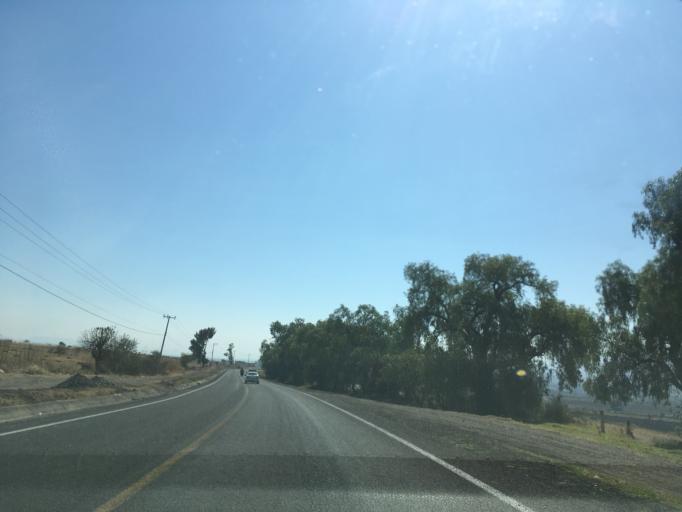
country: MX
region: Michoacan
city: Indaparapeo
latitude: 19.7917
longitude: -100.9595
